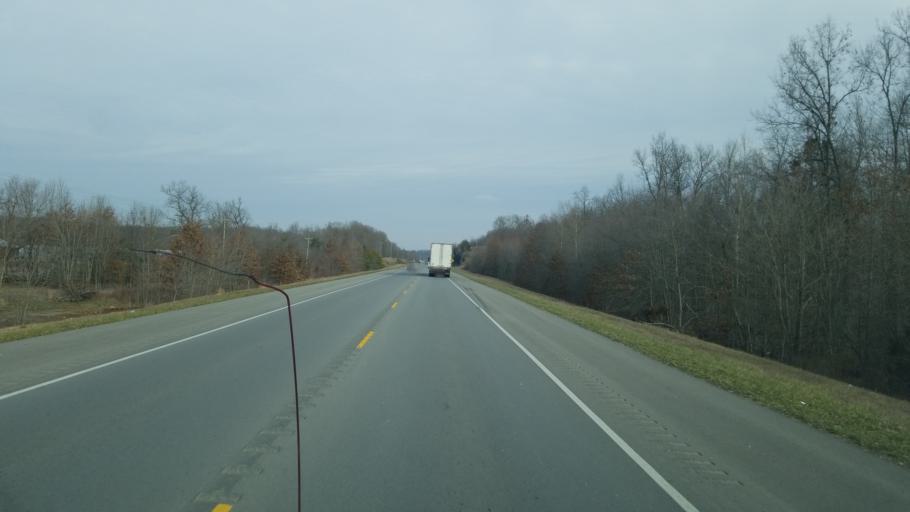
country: US
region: Kentucky
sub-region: Boyle County
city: Junction City
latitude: 37.5508
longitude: -84.8008
